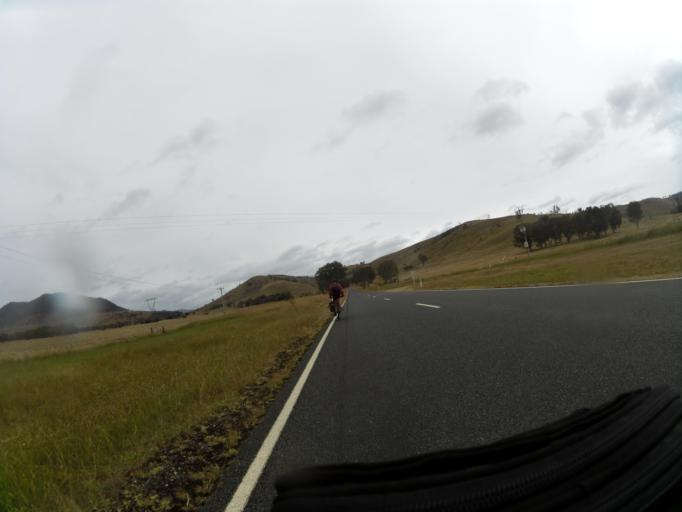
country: AU
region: New South Wales
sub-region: Greater Hume Shire
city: Holbrook
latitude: -36.2062
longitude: 147.7403
